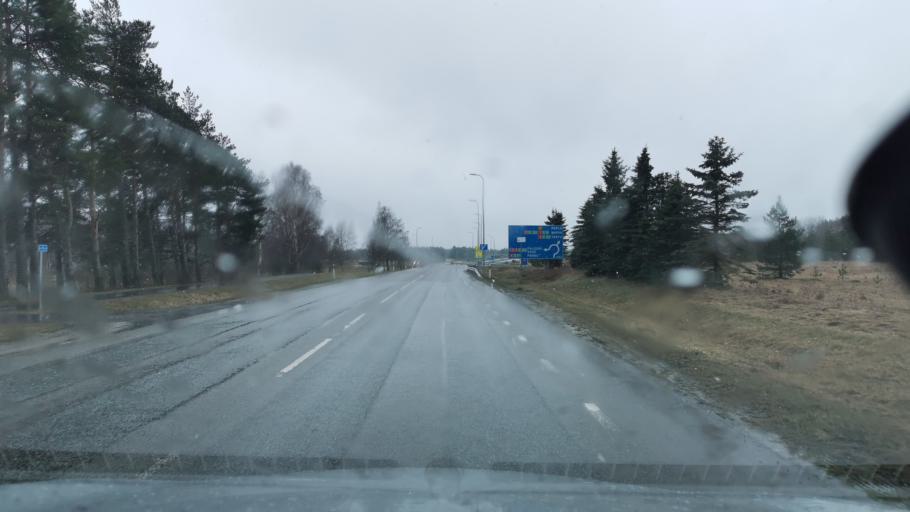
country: EE
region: Harju
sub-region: Kiili vald
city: Kiili
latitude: 59.3271
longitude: 24.7708
